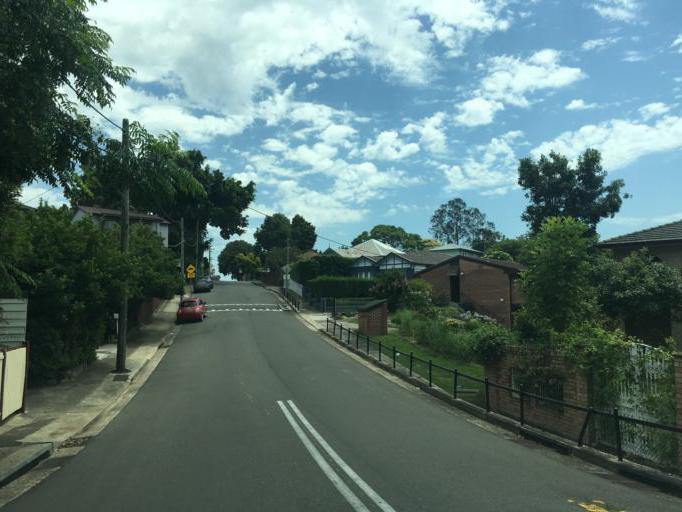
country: AU
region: New South Wales
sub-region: Hunters Hill
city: Gladesville
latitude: -33.8317
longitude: 151.1302
